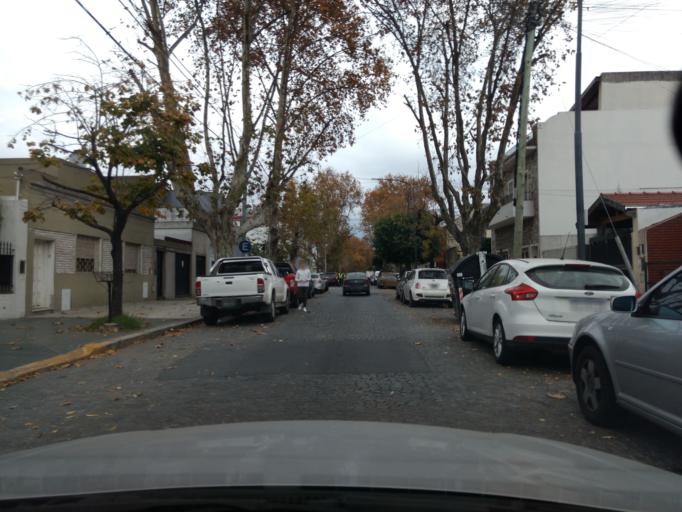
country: AR
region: Buenos Aires F.D.
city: Villa Santa Rita
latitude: -34.6261
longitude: -58.5204
